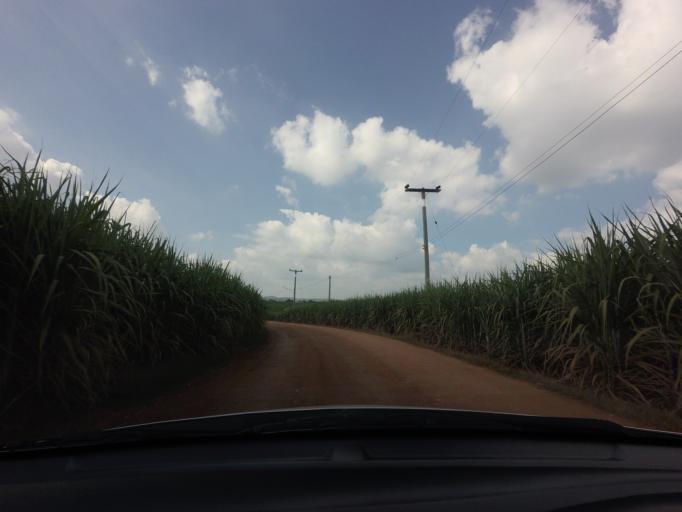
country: TH
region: Nakhon Ratchasima
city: Wang Nam Khiao
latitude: 14.5145
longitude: 101.6317
